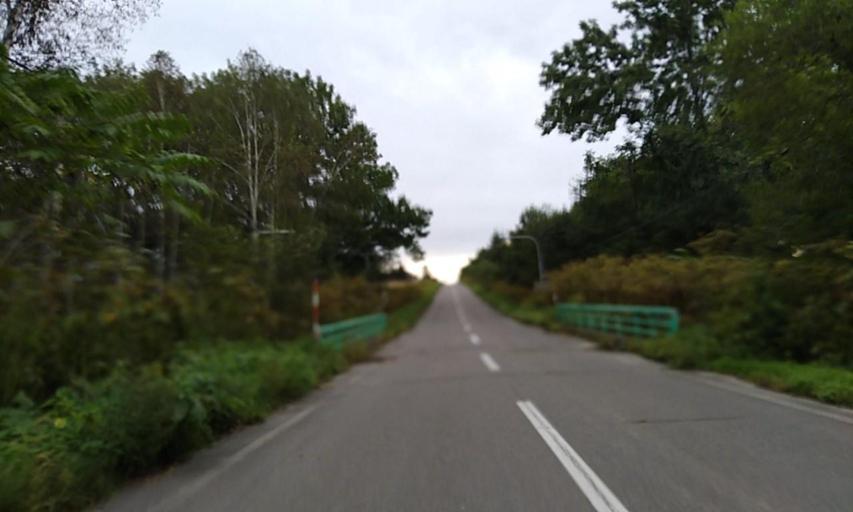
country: JP
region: Hokkaido
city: Obihiro
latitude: 42.6649
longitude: 143.0680
